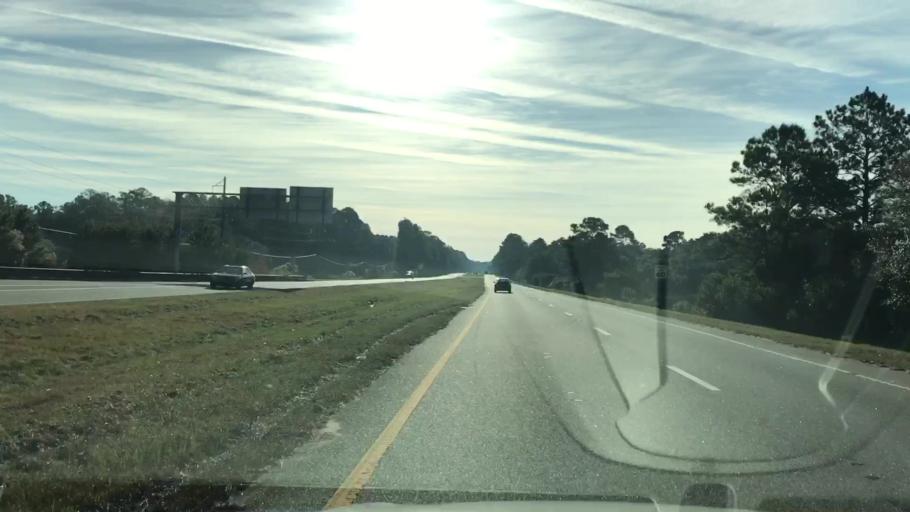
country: US
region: South Carolina
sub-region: Hampton County
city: Yemassee
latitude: 32.5986
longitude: -80.7572
